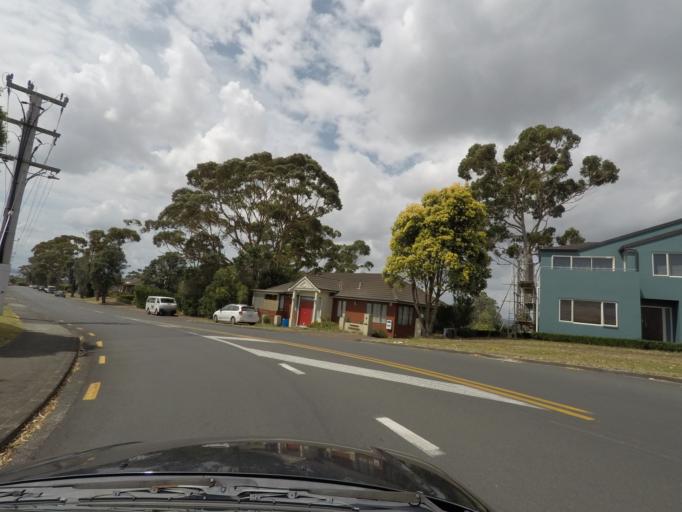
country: NZ
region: Auckland
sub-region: Auckland
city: Waitakere
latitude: -36.9008
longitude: 174.6420
